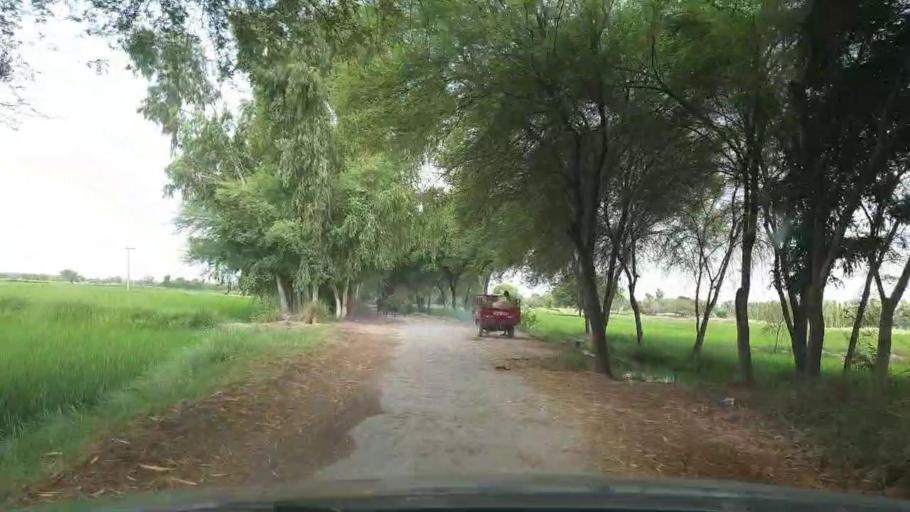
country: PK
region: Sindh
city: Ratodero
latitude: 27.8579
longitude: 68.2951
